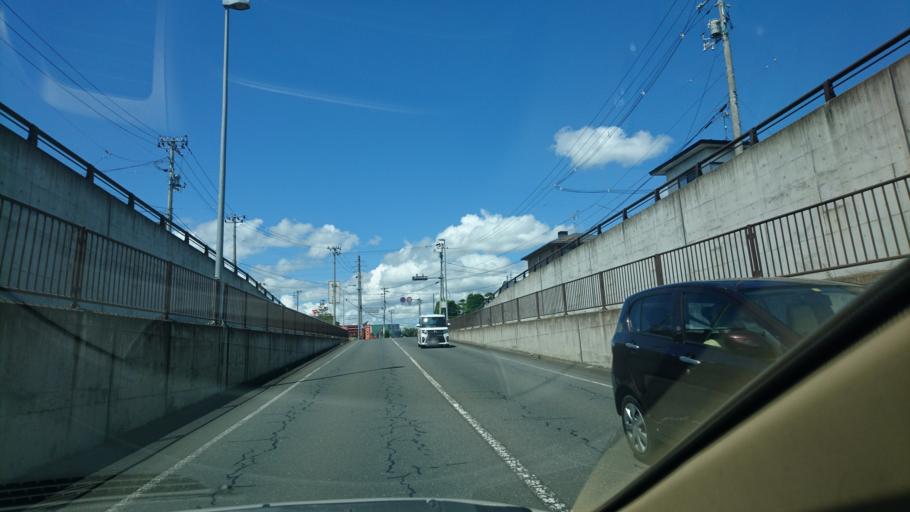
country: JP
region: Iwate
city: Kitakami
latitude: 39.2951
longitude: 141.1109
